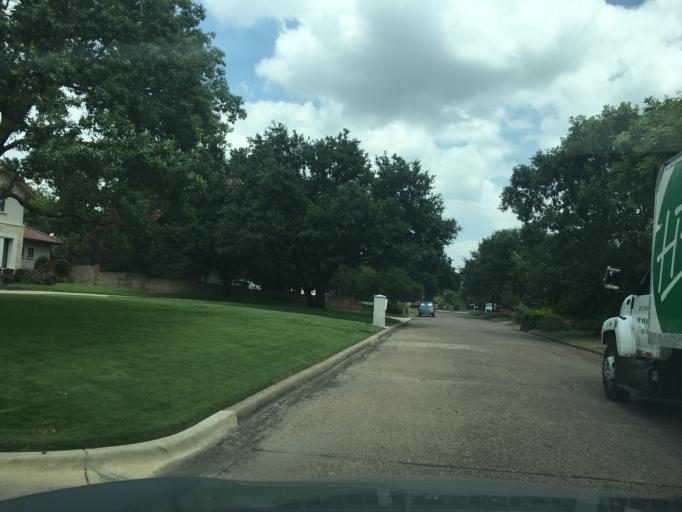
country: US
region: Texas
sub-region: Dallas County
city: University Park
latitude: 32.8932
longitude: -96.8324
